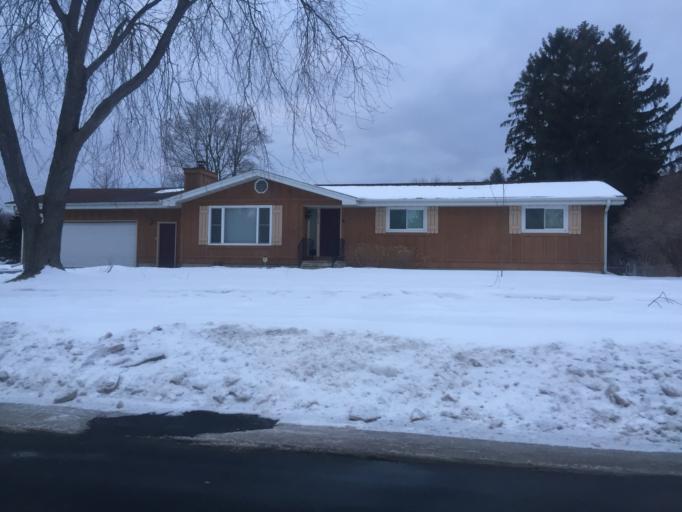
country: US
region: Michigan
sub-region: Menominee County
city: Menominee
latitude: 45.0861
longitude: -87.6115
